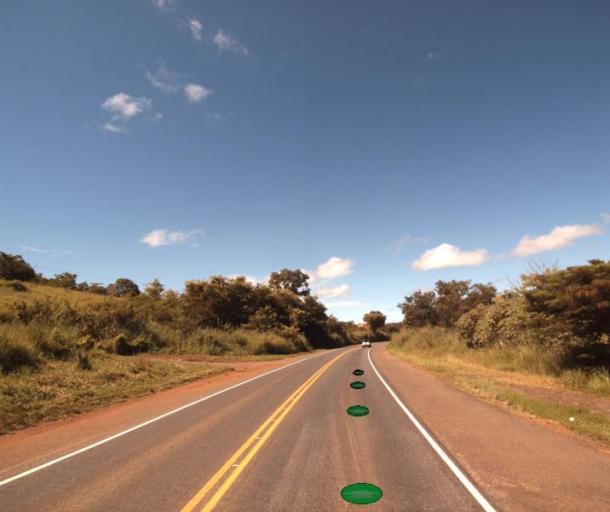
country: BR
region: Goias
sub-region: Rialma
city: Rialma
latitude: -15.2601
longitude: -49.5468
